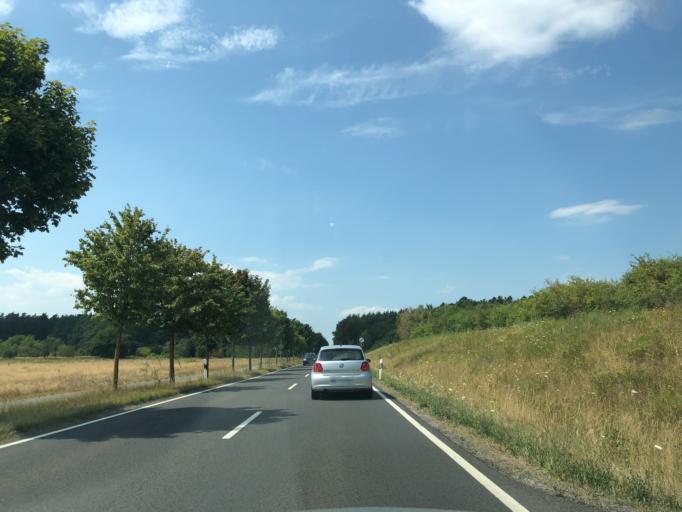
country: DE
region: Hesse
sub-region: Regierungsbezirk Darmstadt
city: Babenhausen
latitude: 49.9760
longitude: 8.9349
